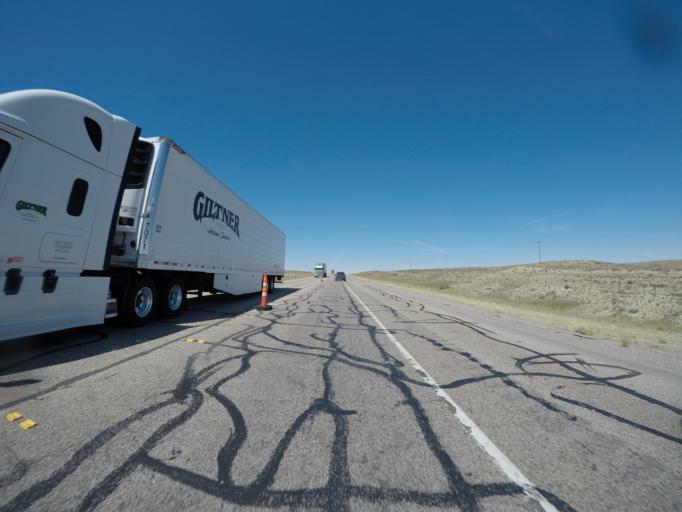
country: US
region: Wyoming
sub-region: Carbon County
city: Saratoga
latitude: 41.7429
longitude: -106.8673
